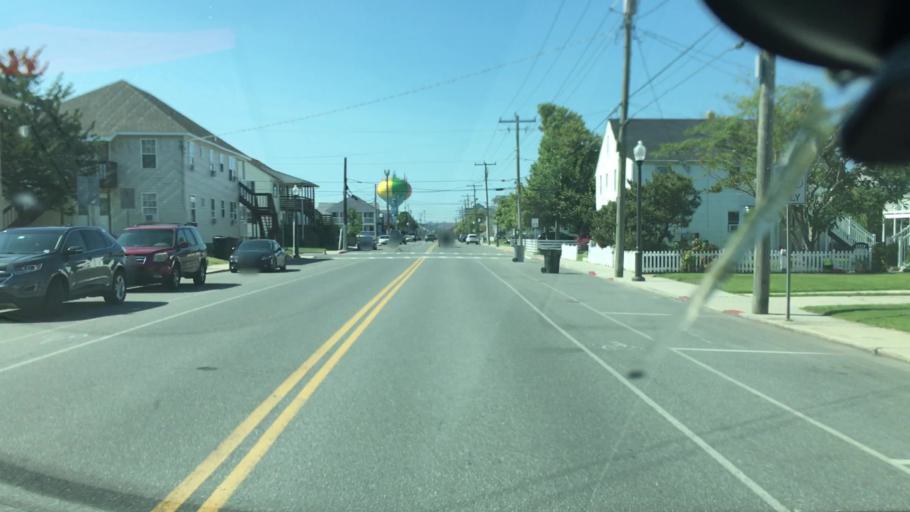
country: US
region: Maryland
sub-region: Worcester County
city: Ocean City
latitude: 38.3385
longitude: -75.0852
